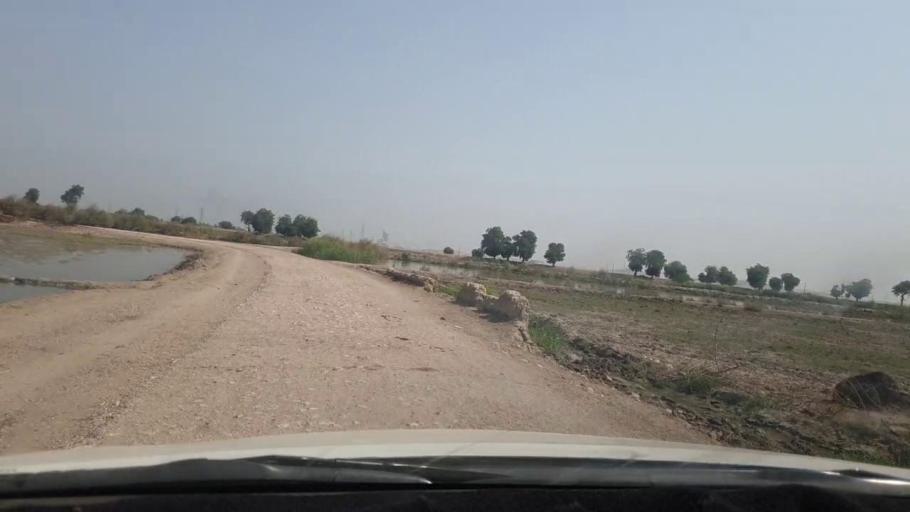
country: PK
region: Sindh
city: Rohri
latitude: 27.6342
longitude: 68.8853
